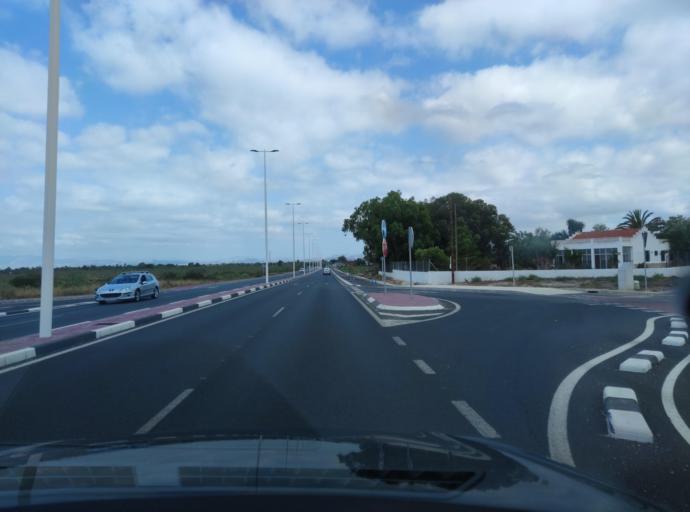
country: ES
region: Valencia
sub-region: Provincia de Alicante
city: Santa Pola
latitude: 38.2127
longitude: -0.5904
